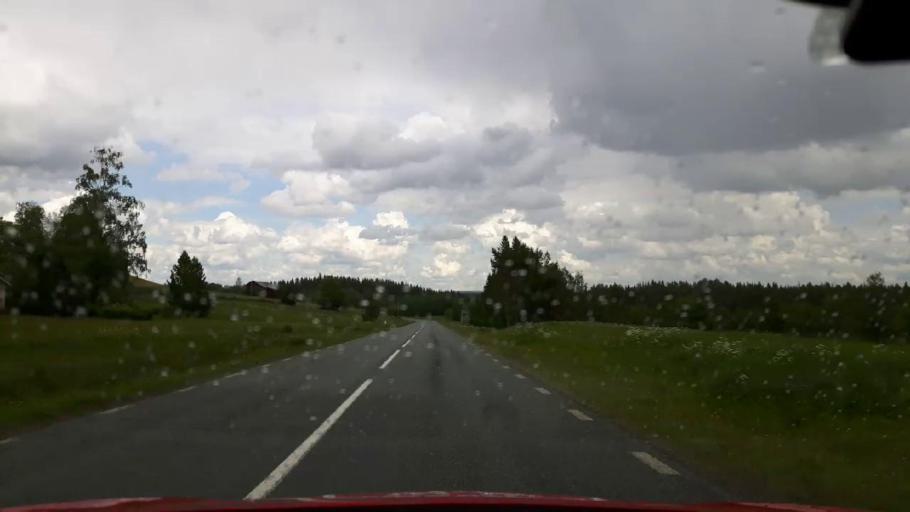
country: SE
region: Jaemtland
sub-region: Krokoms Kommun
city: Krokom
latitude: 63.4918
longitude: 14.2093
